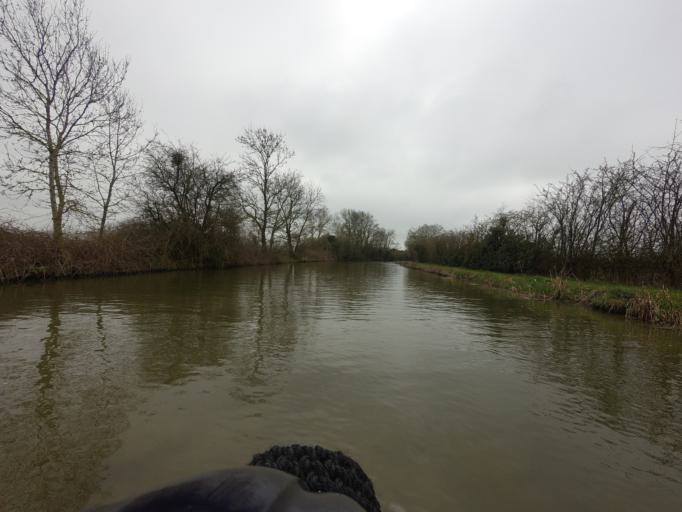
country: GB
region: England
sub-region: Central Bedfordshire
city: Leighton Buzzard
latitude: 51.8832
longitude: -0.6559
